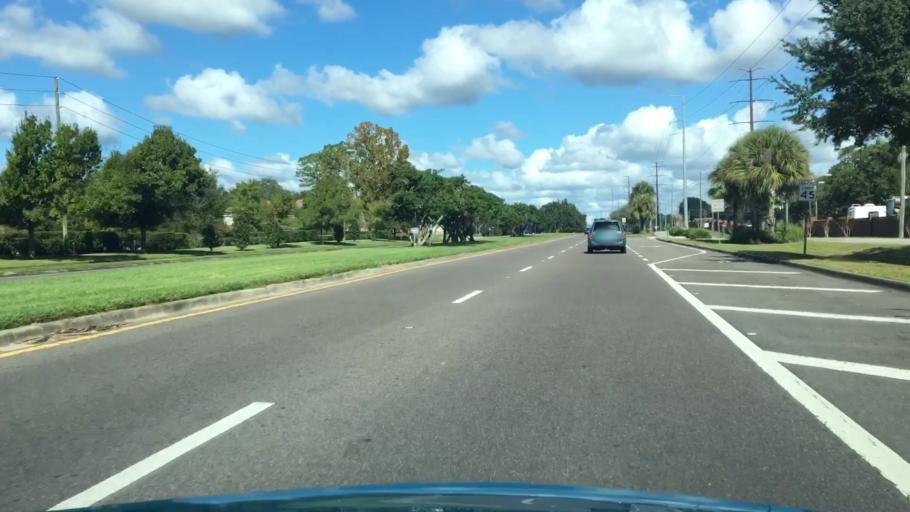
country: US
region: Florida
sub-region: Seminole County
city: Heathrow
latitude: 28.7575
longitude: -81.3470
